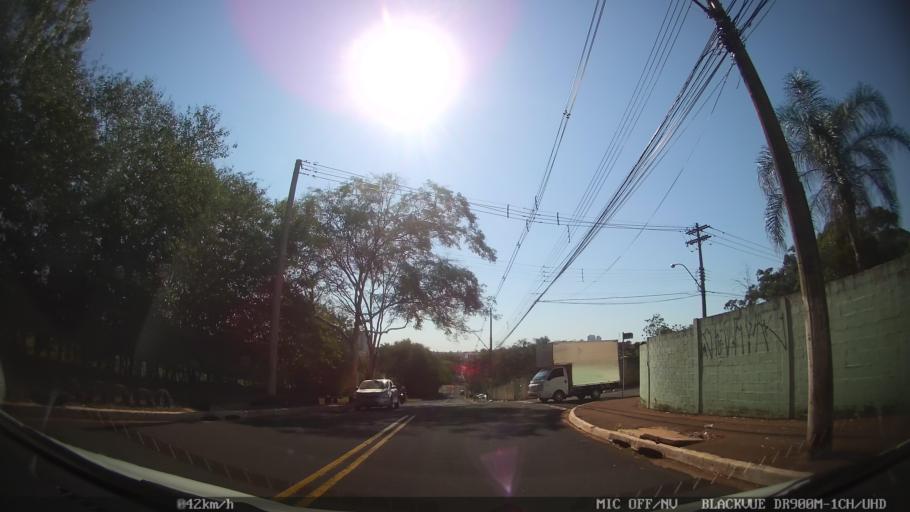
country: BR
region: Sao Paulo
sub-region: Ribeirao Preto
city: Ribeirao Preto
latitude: -21.2106
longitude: -47.8256
